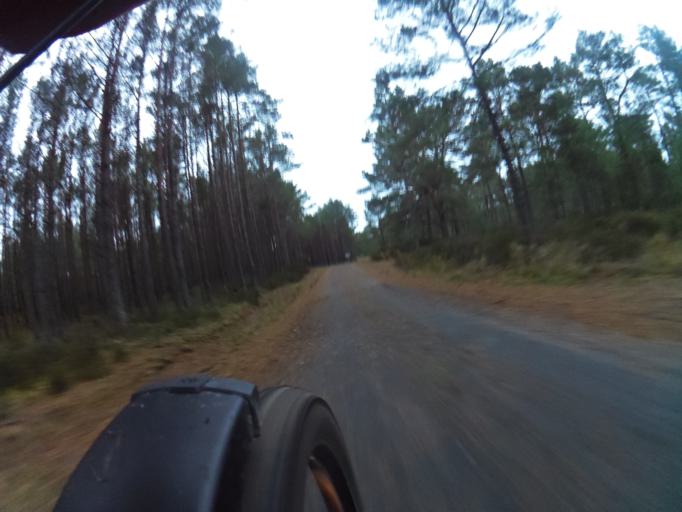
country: PL
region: Pomeranian Voivodeship
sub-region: Powiat wejherowski
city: Choczewo
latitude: 54.7975
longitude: 17.7795
